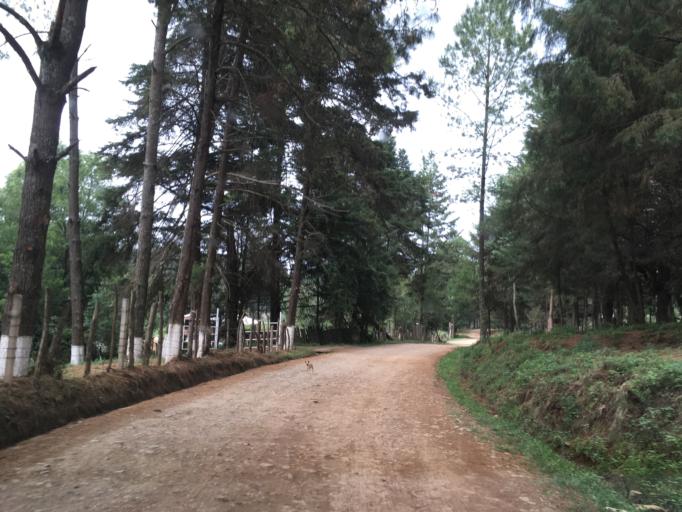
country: MX
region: Michoacan
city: Acuitzio del Canje
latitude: 19.5103
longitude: -101.2152
